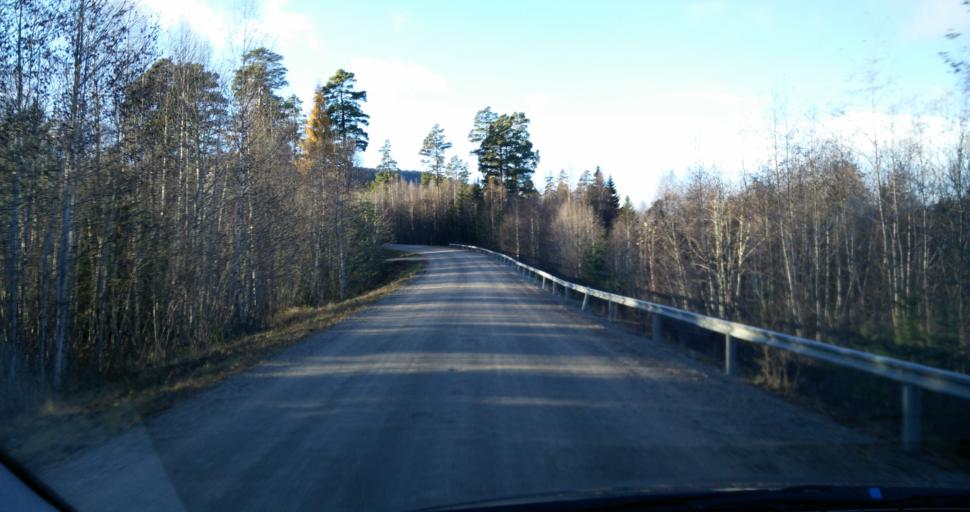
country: SE
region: Gaevleborg
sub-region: Nordanstigs Kommun
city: Bergsjoe
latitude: 62.0582
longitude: 16.7971
